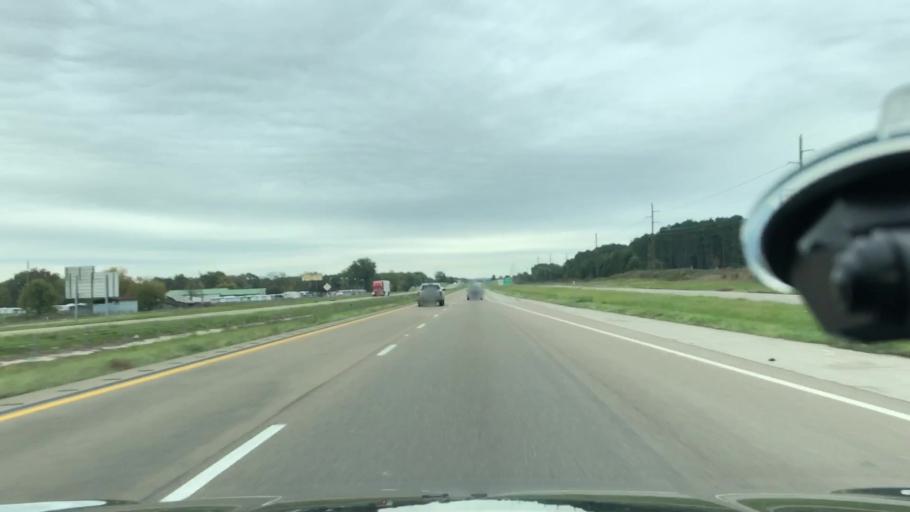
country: US
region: Texas
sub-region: Titus County
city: Mount Pleasant
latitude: 33.1591
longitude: -95.0684
